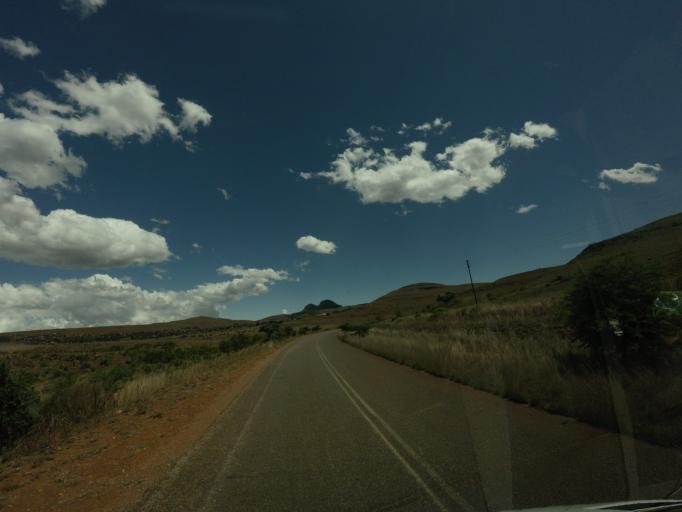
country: ZA
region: Limpopo
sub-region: Mopani District Municipality
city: Hoedspruit
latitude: -24.6010
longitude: 30.7892
